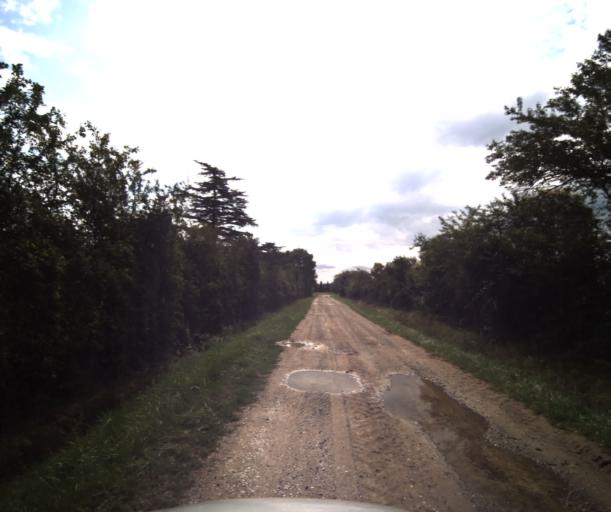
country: FR
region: Midi-Pyrenees
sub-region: Departement de la Haute-Garonne
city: Lacasse
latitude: 43.3941
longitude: 1.2363
